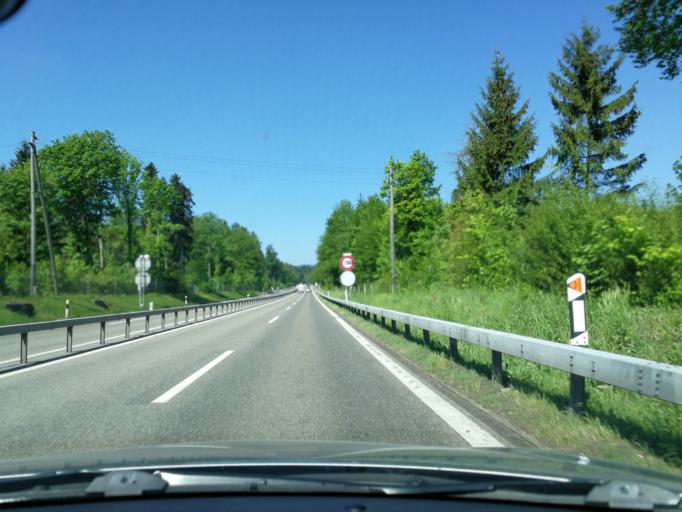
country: CH
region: Zurich
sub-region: Bezirk Hinwil
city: Binzikon
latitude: 47.2892
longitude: 8.7591
